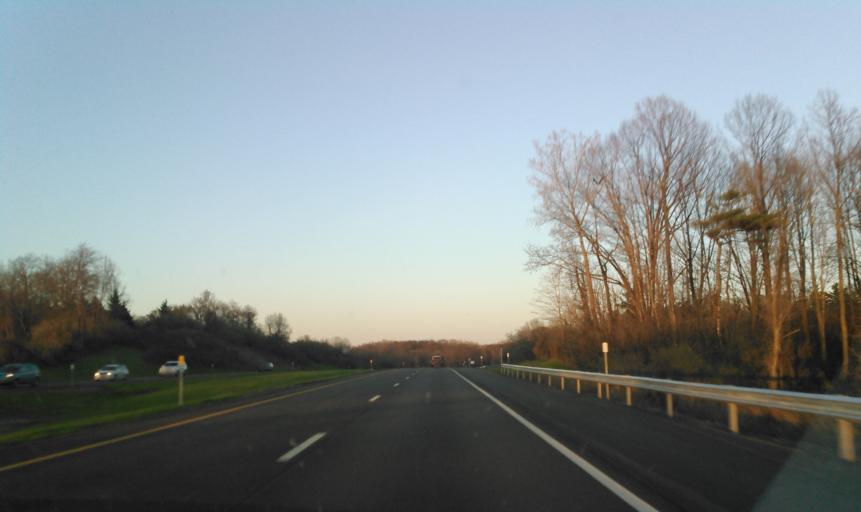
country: US
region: New York
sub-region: Ontario County
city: Geneva
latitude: 42.9582
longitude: -76.9539
